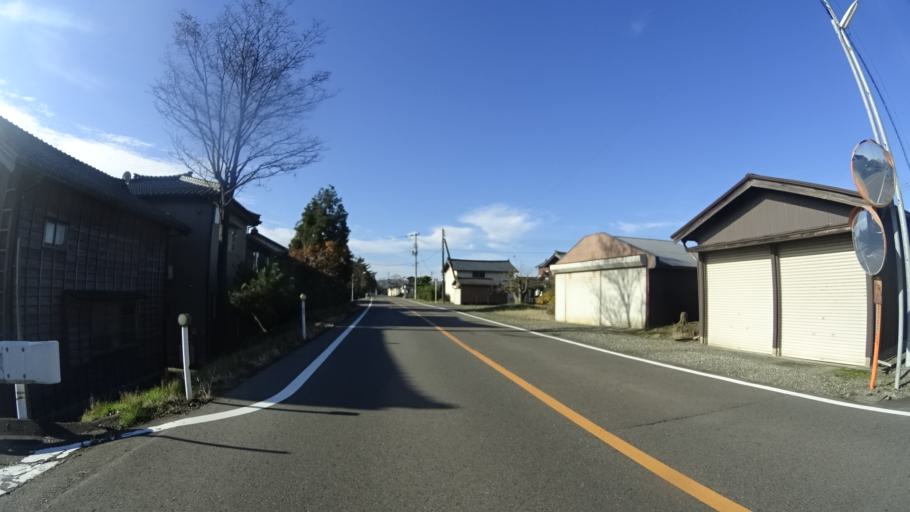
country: JP
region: Niigata
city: Yoshida-kasugacho
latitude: 37.5951
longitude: 138.8459
